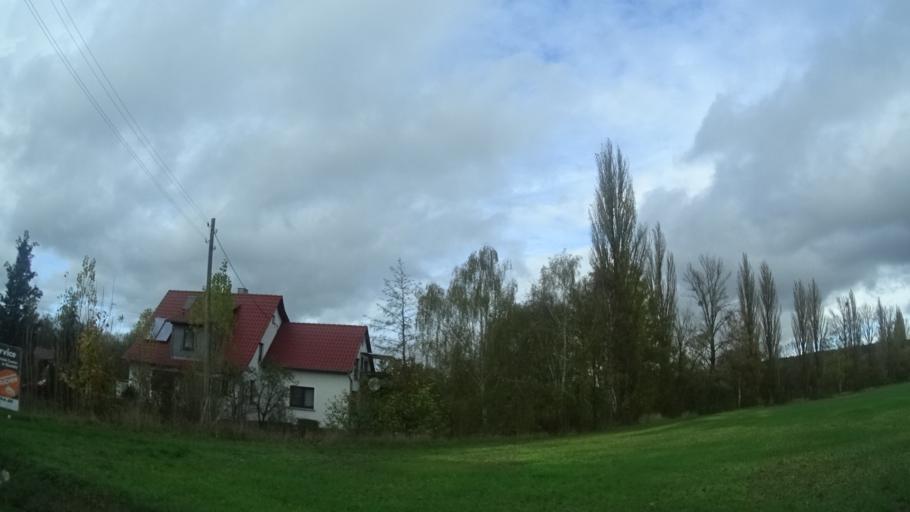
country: DE
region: Thuringia
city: Romhild
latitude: 50.4008
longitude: 10.5483
